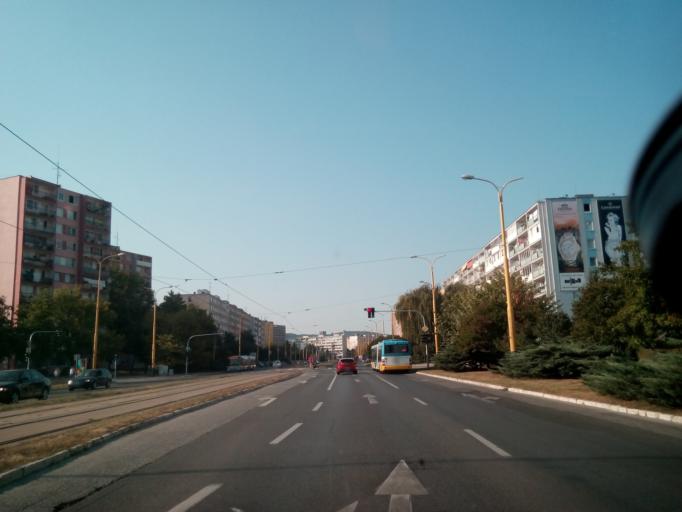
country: SK
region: Kosicky
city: Kosice
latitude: 48.7146
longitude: 21.2352
